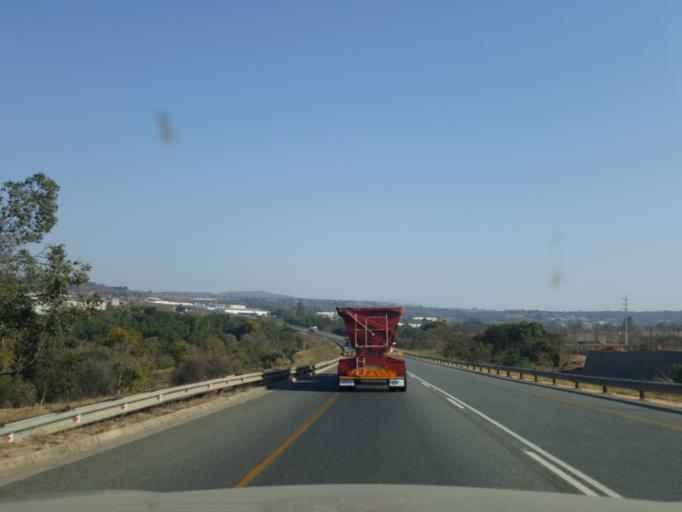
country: ZA
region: Mpumalanga
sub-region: Ehlanzeni District
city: Nelspruit
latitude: -25.4363
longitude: 30.9756
